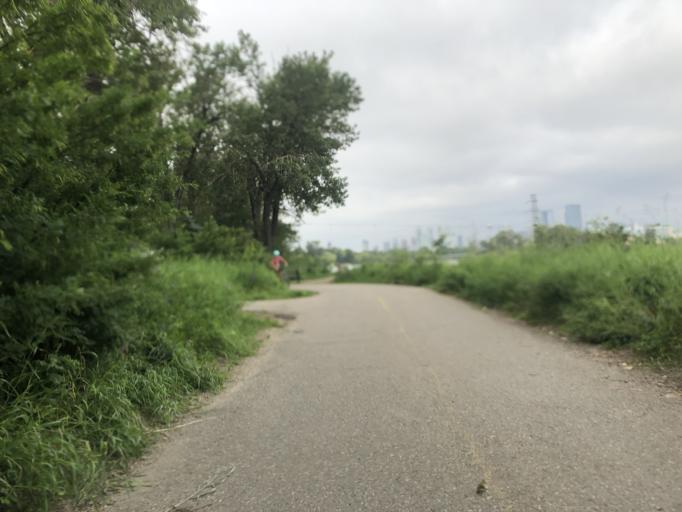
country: CA
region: Alberta
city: Calgary
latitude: 51.0435
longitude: -114.0197
